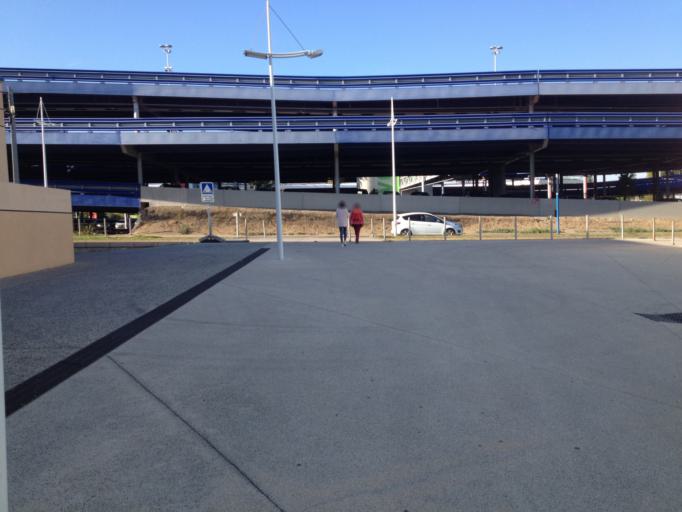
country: FR
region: Languedoc-Roussillon
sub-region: Departement de l'Herault
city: Castelnau-le-Lez
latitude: 43.6042
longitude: 3.9188
